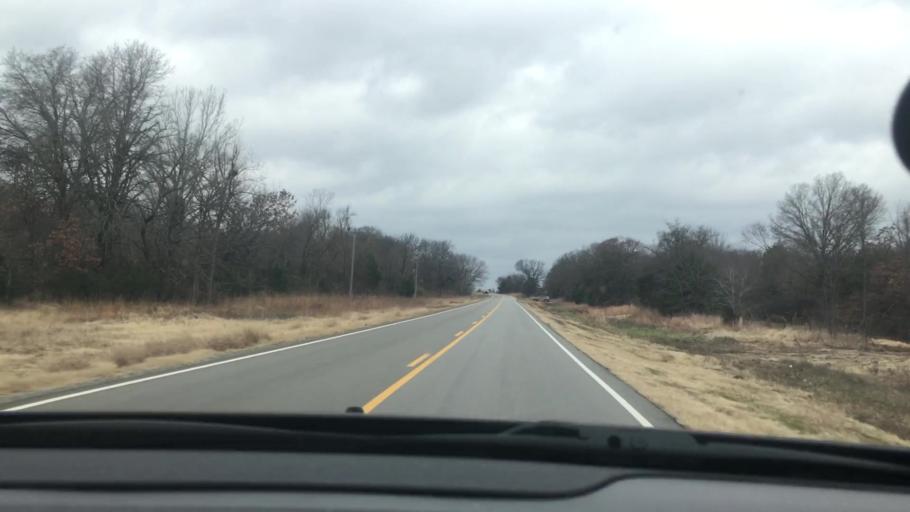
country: US
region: Oklahoma
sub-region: Atoka County
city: Atoka
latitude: 34.3791
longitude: -96.2827
